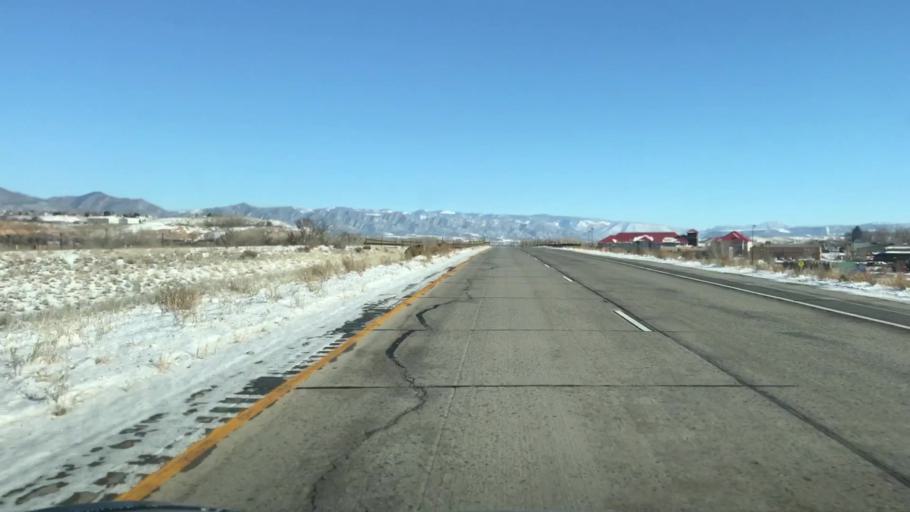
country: US
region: Colorado
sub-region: Garfield County
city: Rifle
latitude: 39.5233
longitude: -107.7797
